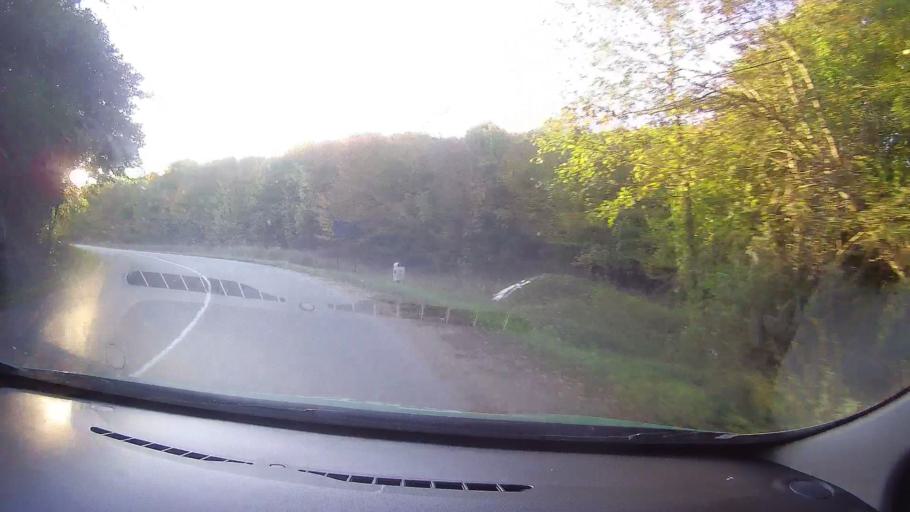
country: RO
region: Timis
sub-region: Comuna Dumbrava
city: Dumbrava
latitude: 45.7578
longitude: 22.1087
